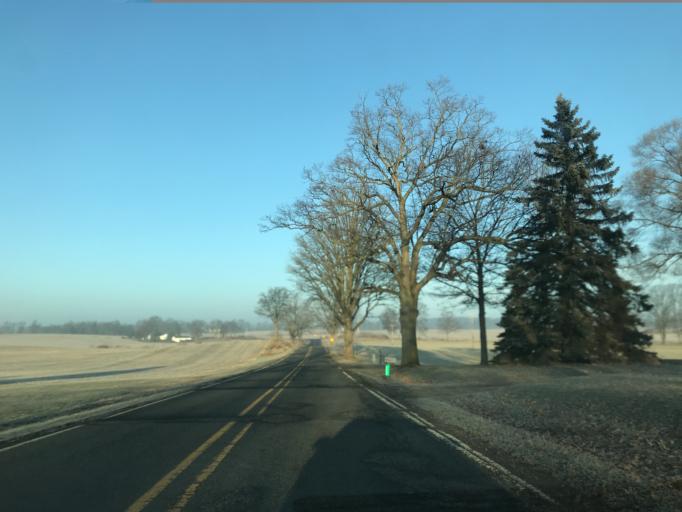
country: US
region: Michigan
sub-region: Ingham County
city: Leslie
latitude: 42.4198
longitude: -84.5139
